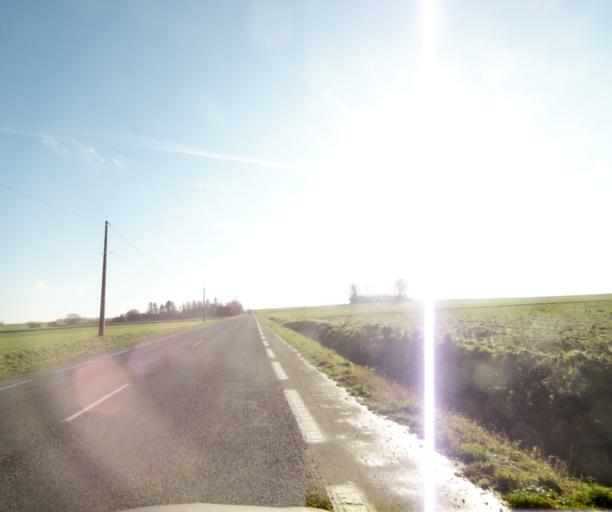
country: FR
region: Nord-Pas-de-Calais
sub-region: Departement du Nord
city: Preseau
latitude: 50.3248
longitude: 3.5627
